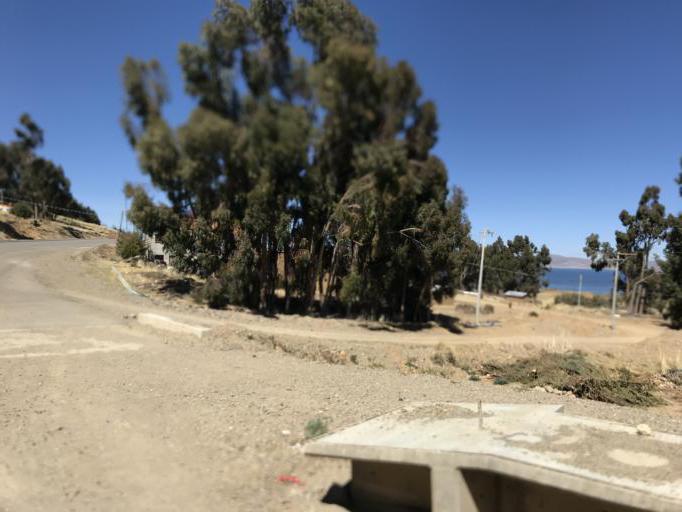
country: BO
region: La Paz
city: Huarina
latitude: -16.2138
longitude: -68.6519
